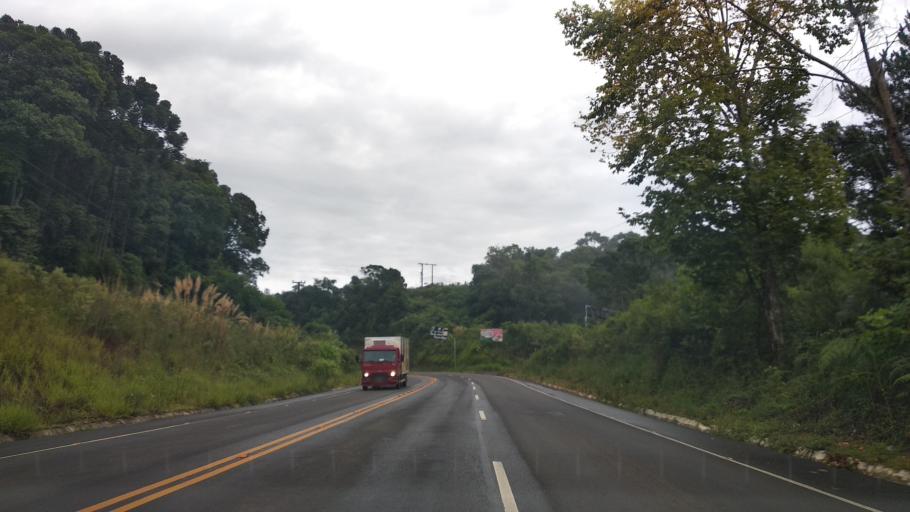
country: BR
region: Santa Catarina
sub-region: Videira
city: Videira
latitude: -27.0520
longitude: -51.1782
